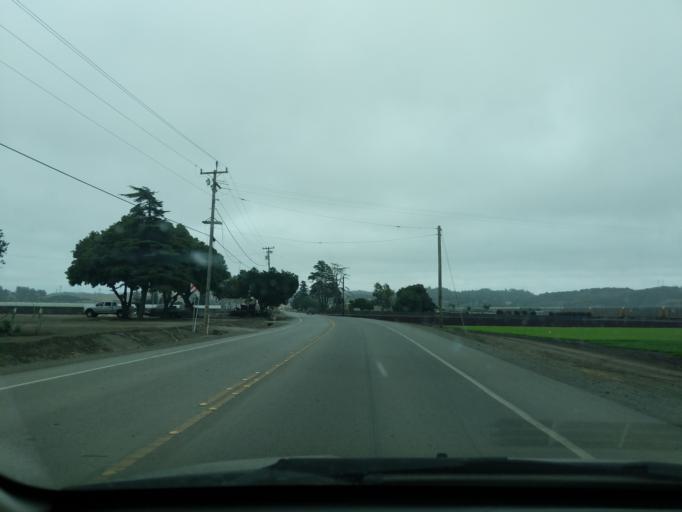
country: US
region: California
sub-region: San Benito County
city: Aromas
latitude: 36.8985
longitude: -121.6859
